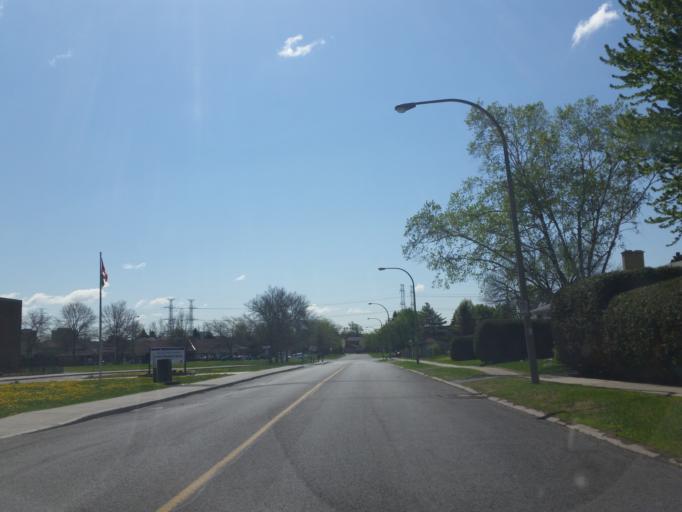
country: CA
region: Ontario
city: Ottawa
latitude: 45.3498
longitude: -75.7178
